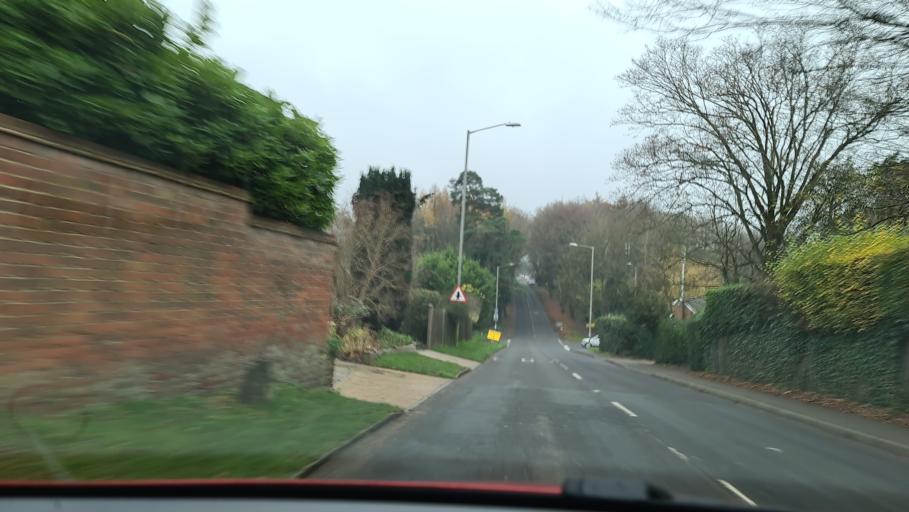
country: GB
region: England
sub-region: Buckinghamshire
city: Beaconsfield
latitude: 51.6404
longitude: -0.6934
